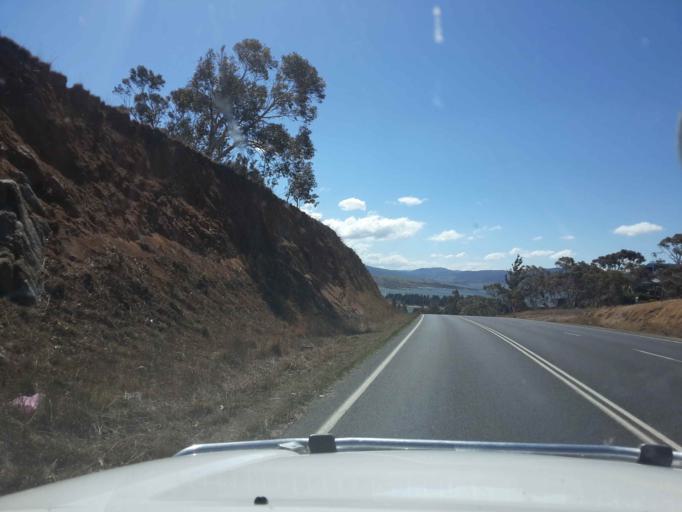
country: AU
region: New South Wales
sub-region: Snowy River
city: Jindabyne
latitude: -36.4218
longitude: 148.6102
